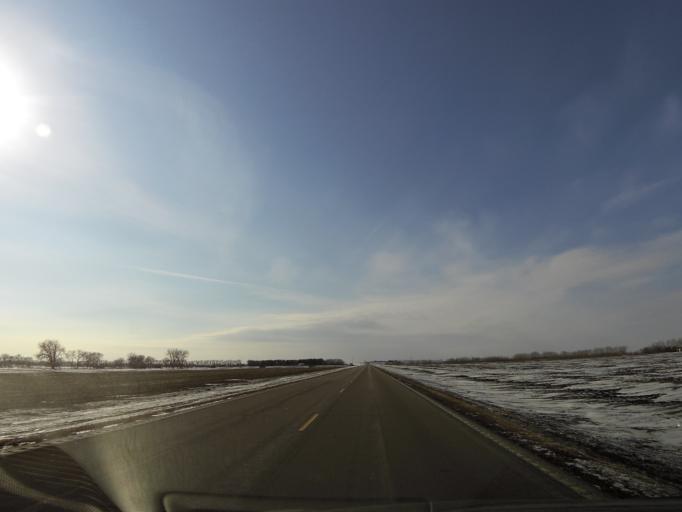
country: US
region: North Dakota
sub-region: Walsh County
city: Grafton
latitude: 48.4121
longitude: -97.1711
